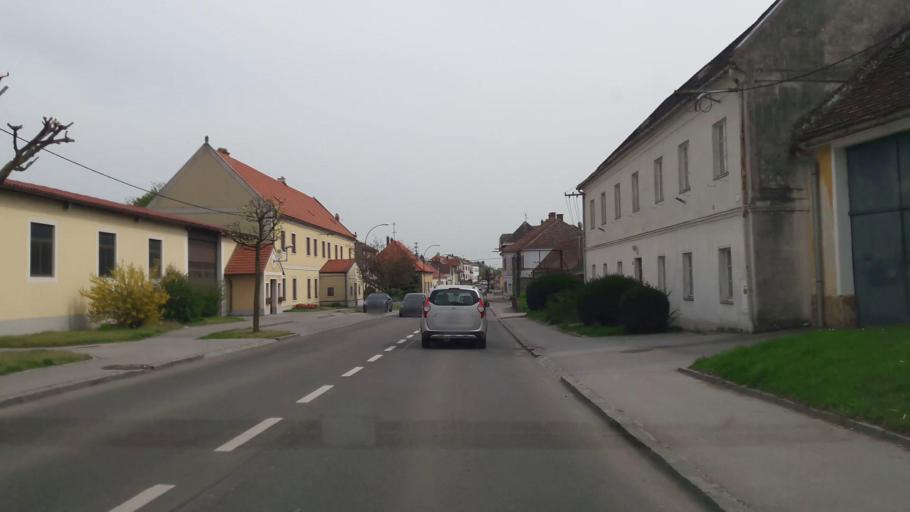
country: AT
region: Lower Austria
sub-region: Politischer Bezirk Bruck an der Leitha
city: Wolfsthal
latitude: 48.1365
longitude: 17.0078
